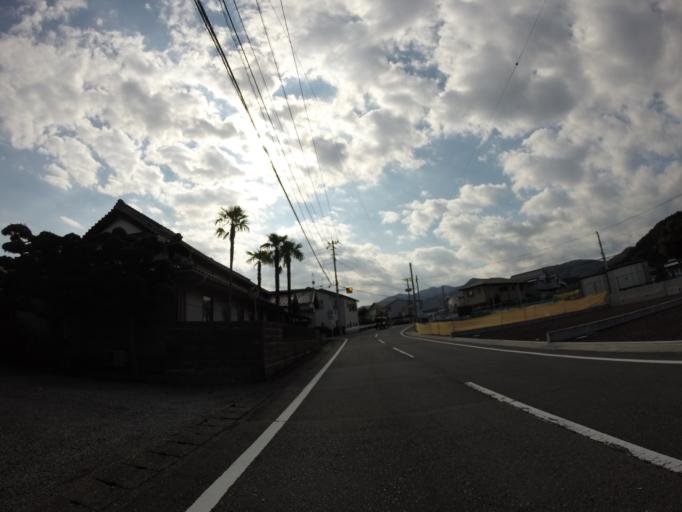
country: JP
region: Shizuoka
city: Fujinomiya
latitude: 35.1732
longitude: 138.6337
